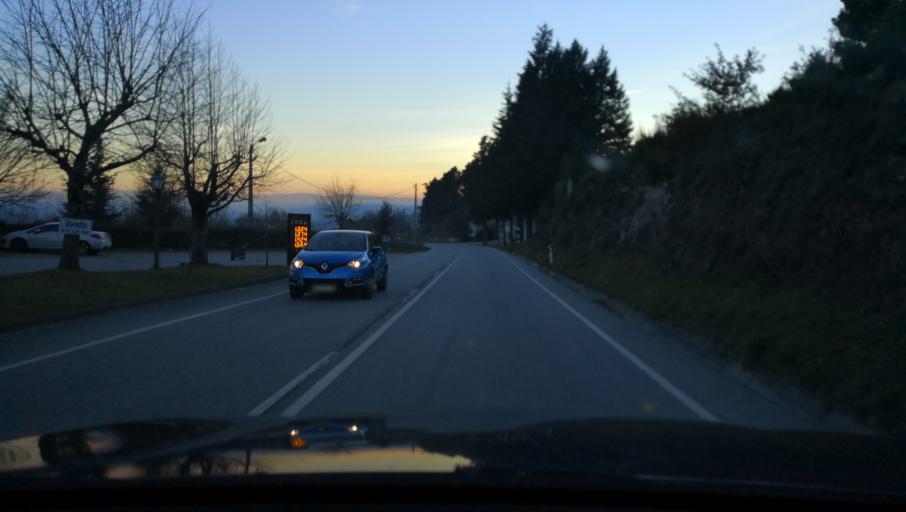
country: PT
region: Vila Real
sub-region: Vila Real
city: Vila Real
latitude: 41.3892
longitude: -7.7028
